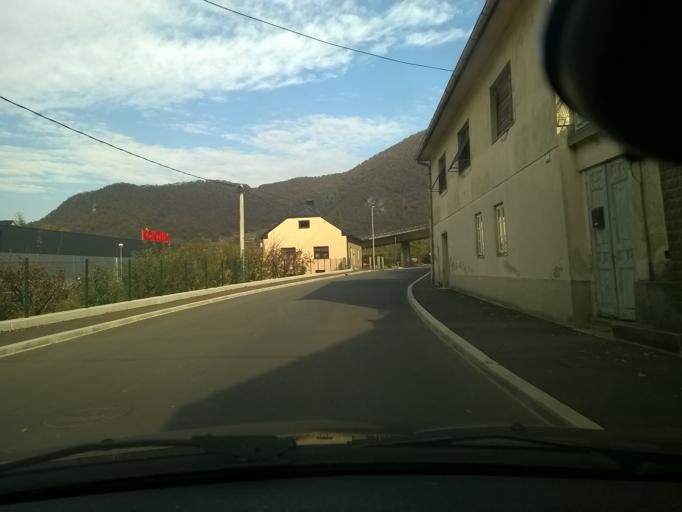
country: HR
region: Krapinsko-Zagorska
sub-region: Grad Krapina
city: Krapina
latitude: 46.1711
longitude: 15.8640
